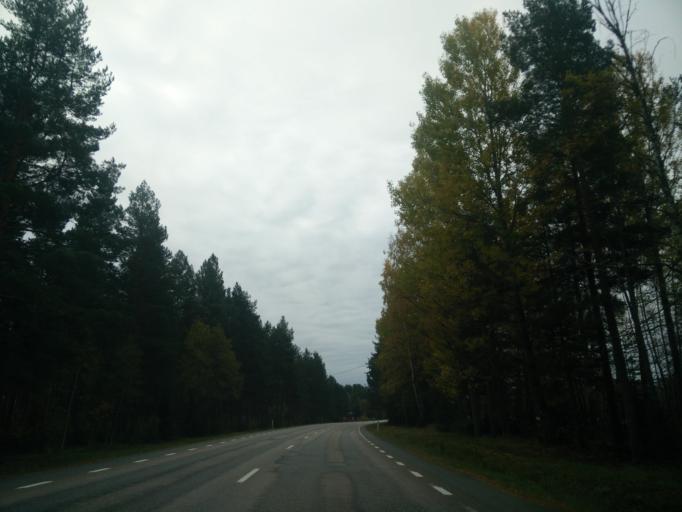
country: SE
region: Gaevleborg
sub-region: Gavle Kommun
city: Norrsundet
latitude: 60.8768
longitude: 17.1623
